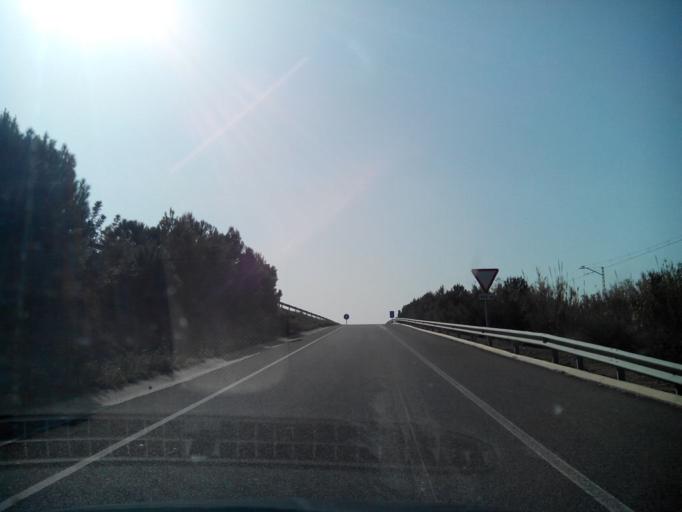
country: ES
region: Catalonia
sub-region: Provincia de Tarragona
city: Alcover
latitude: 41.2530
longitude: 1.1732
